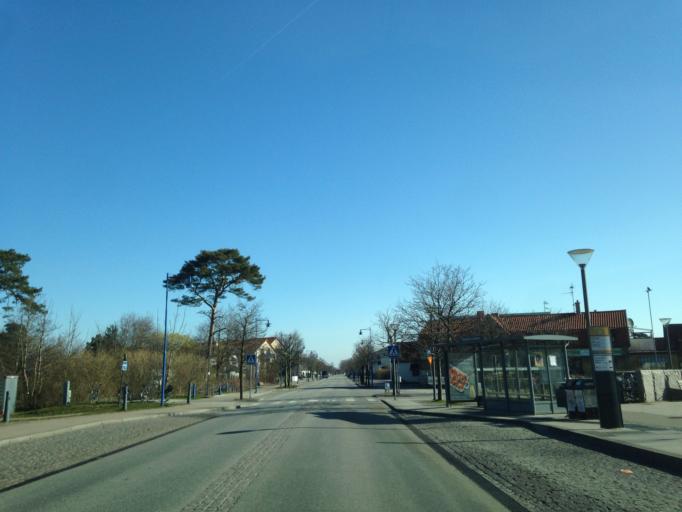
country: SE
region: Skane
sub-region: Vellinge Kommun
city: Hollviken
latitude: 55.4186
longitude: 12.9530
